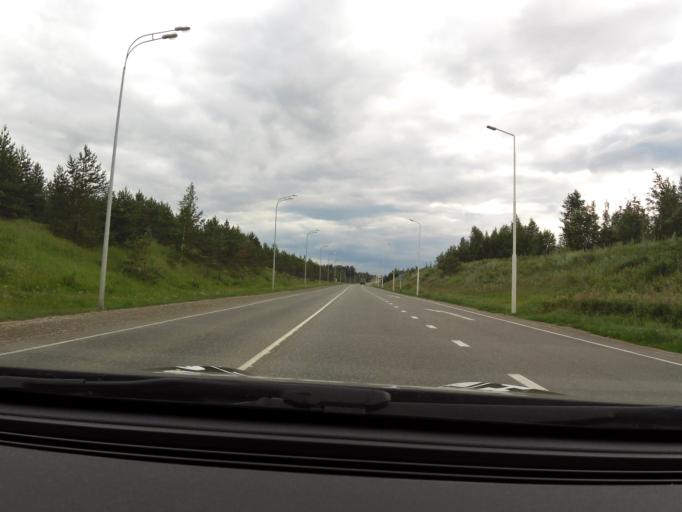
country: RU
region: Tatarstan
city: Sviyazhsk
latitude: 55.7319
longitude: 48.7729
